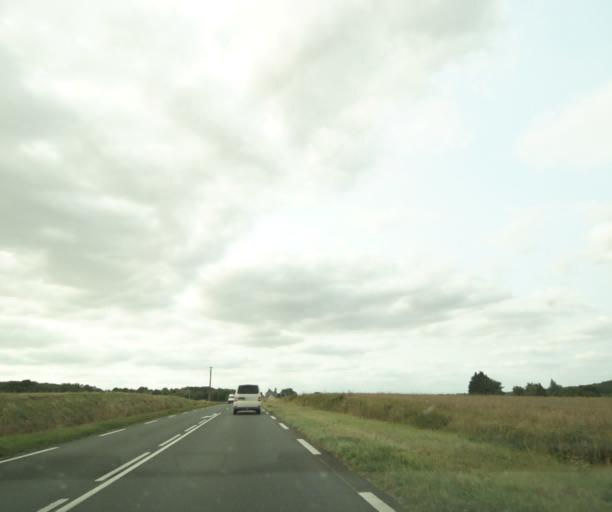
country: FR
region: Centre
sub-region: Departement d'Indre-et-Loire
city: Chambourg-sur-Indre
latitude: 47.1611
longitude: 0.9896
